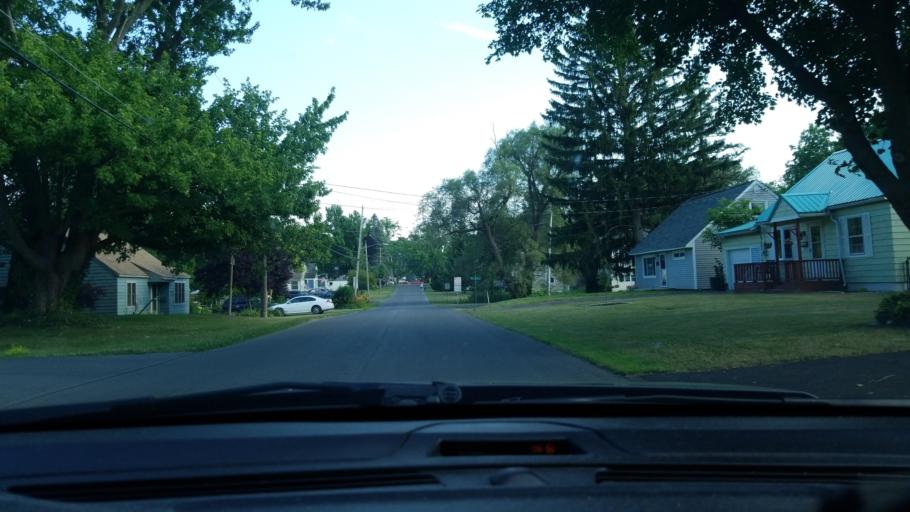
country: US
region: New York
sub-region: Onondaga County
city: North Syracuse
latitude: 43.1417
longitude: -76.1365
